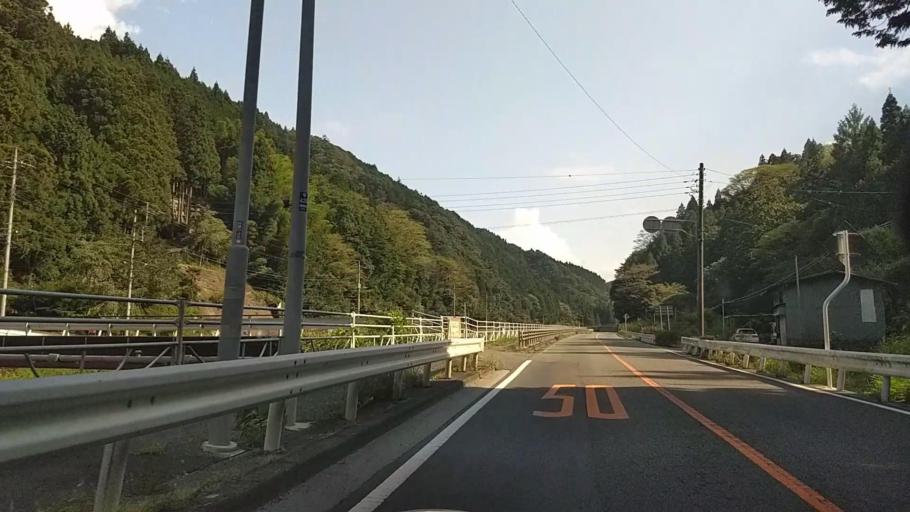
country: JP
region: Shizuoka
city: Fujinomiya
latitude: 35.3476
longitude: 138.4230
